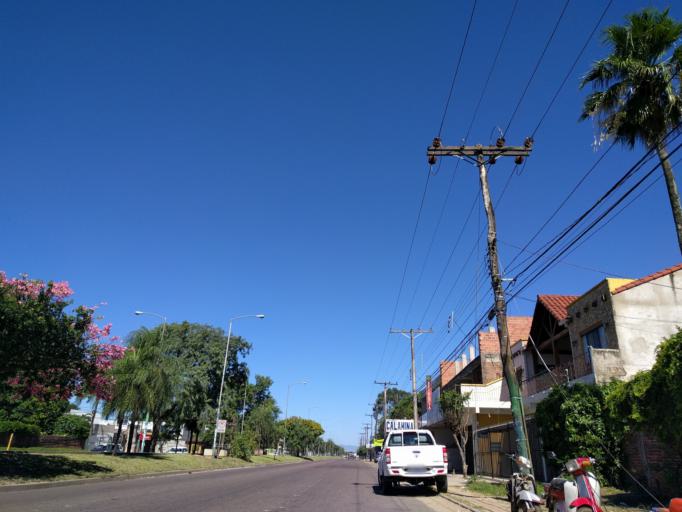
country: BO
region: Santa Cruz
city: Santa Cruz de la Sierra
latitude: -17.8228
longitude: -63.2208
